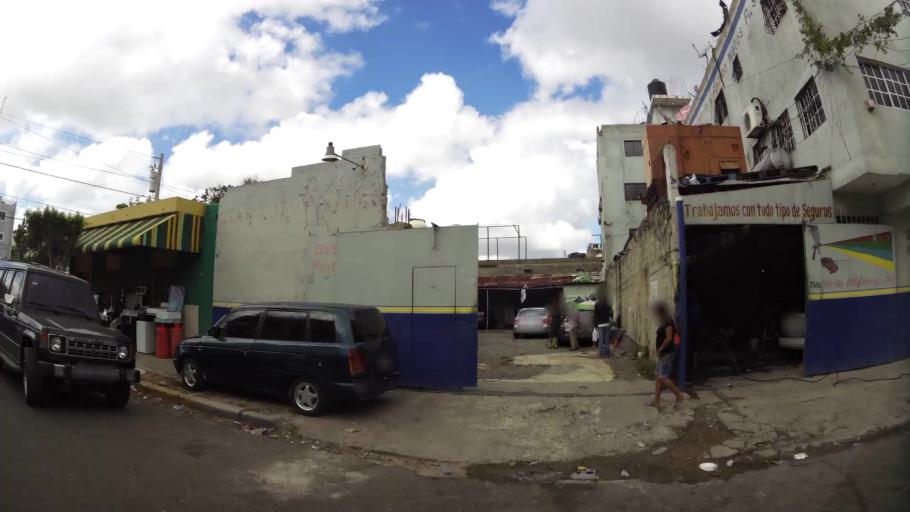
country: DO
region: Nacional
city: San Carlos
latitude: 18.4850
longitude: -69.8969
